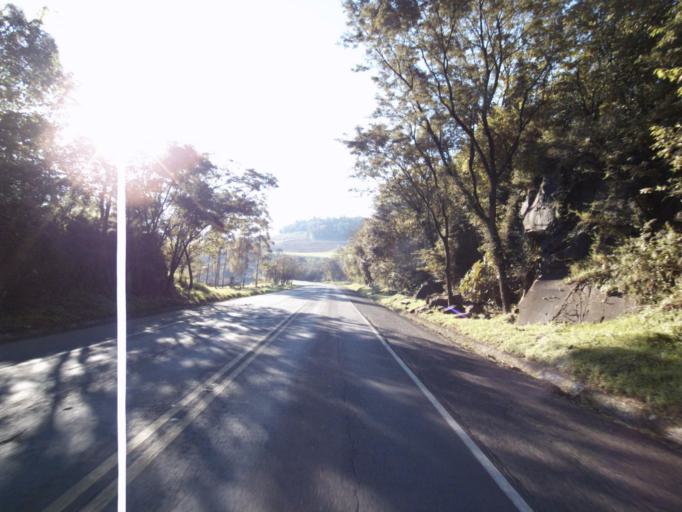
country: BR
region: Santa Catarina
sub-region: Chapeco
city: Chapeco
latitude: -26.9306
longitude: -52.8417
